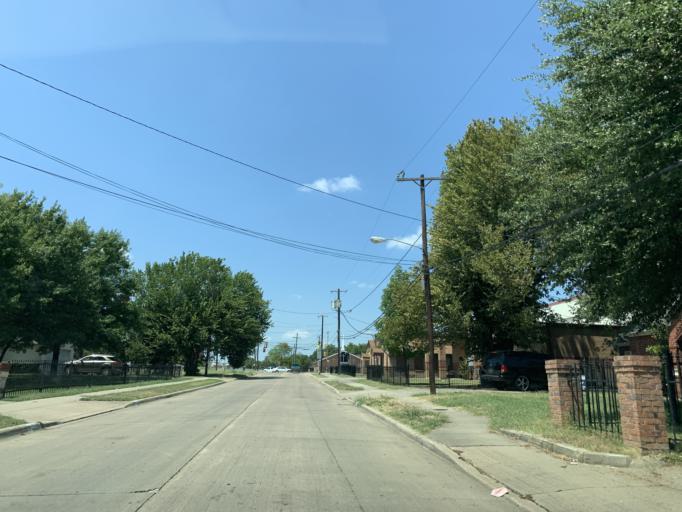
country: US
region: Texas
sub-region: Dallas County
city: Hutchins
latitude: 32.6895
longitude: -96.7794
